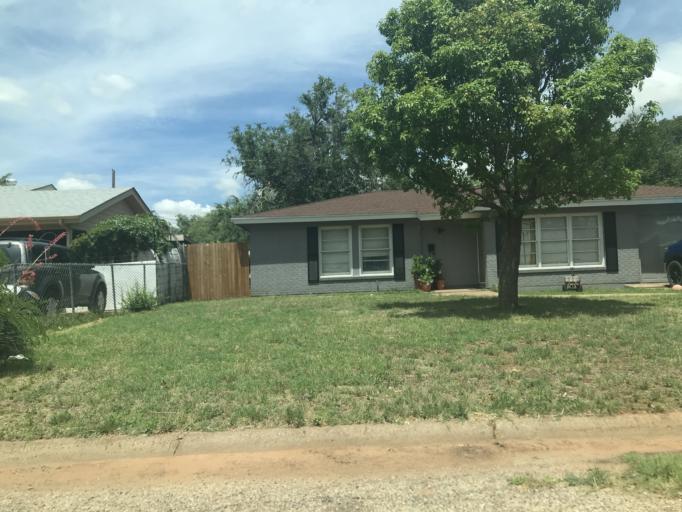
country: US
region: Texas
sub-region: Taylor County
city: Abilene
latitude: 32.4634
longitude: -99.7621
